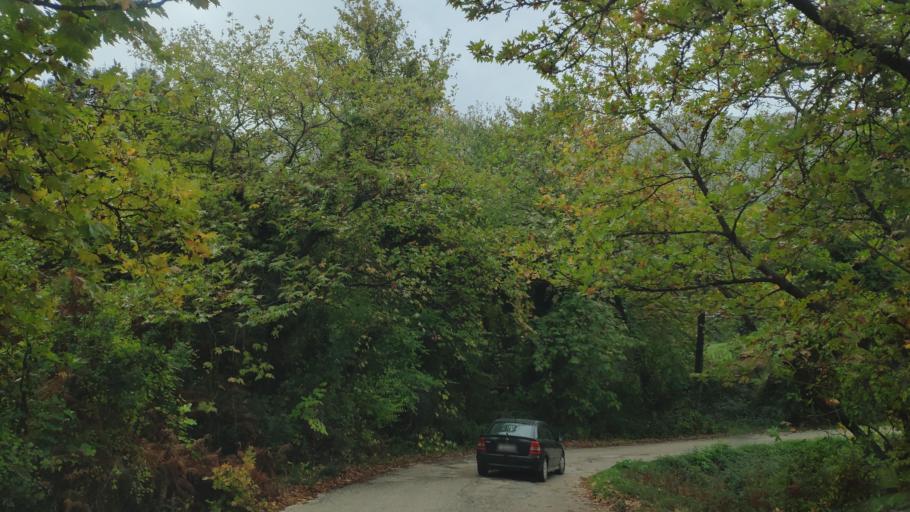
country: GR
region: Epirus
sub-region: Nomos Thesprotias
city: Paramythia
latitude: 39.4707
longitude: 20.6697
